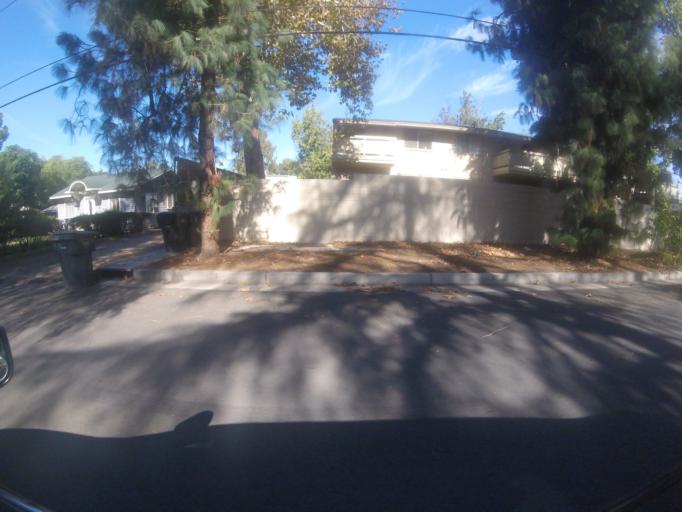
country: US
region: California
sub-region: San Bernardino County
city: Redlands
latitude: 34.0602
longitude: -117.1588
